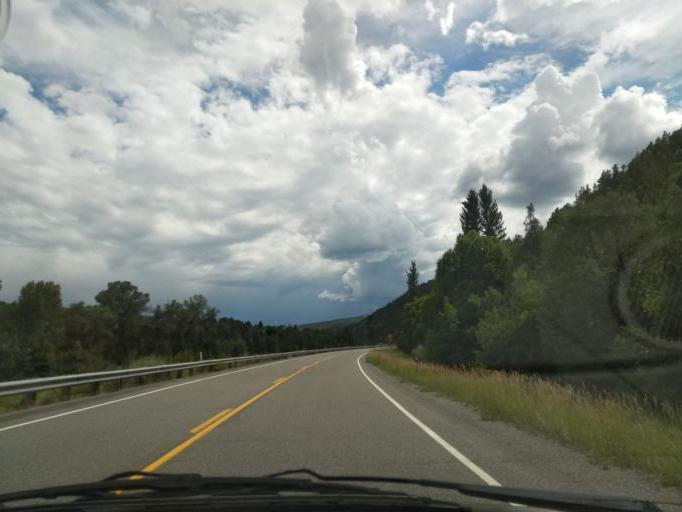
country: US
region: Colorado
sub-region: Delta County
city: Paonia
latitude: 39.0236
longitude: -107.3621
